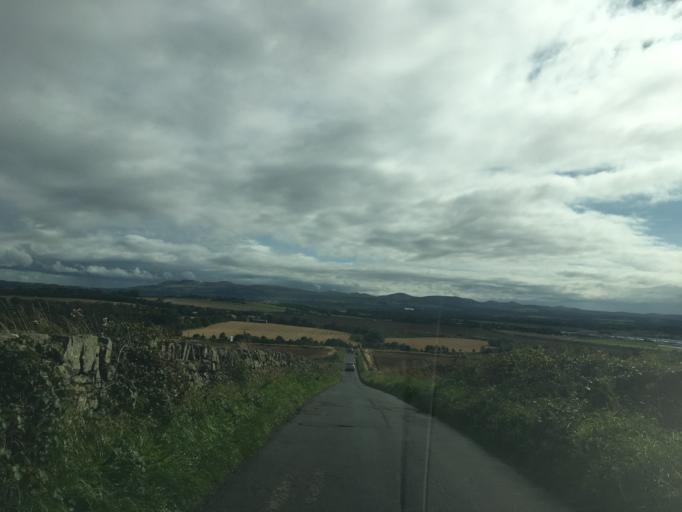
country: GB
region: Scotland
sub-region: Edinburgh
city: Queensferry
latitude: 55.9701
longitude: -3.3520
